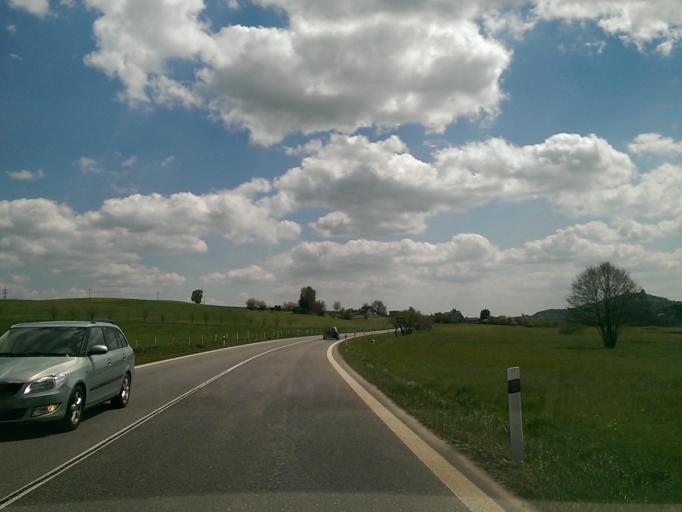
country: CZ
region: Liberecky
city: Rovensko pod Troskami
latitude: 50.5580
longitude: 15.2055
